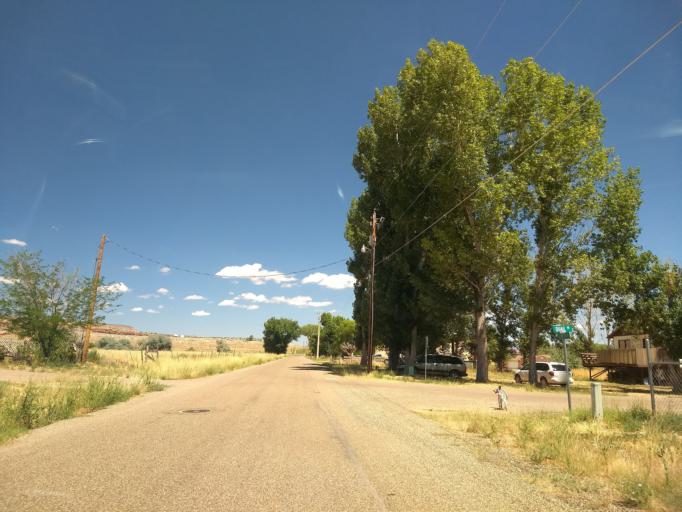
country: US
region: Arizona
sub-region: Coconino County
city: Fredonia
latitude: 36.9419
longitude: -112.5354
